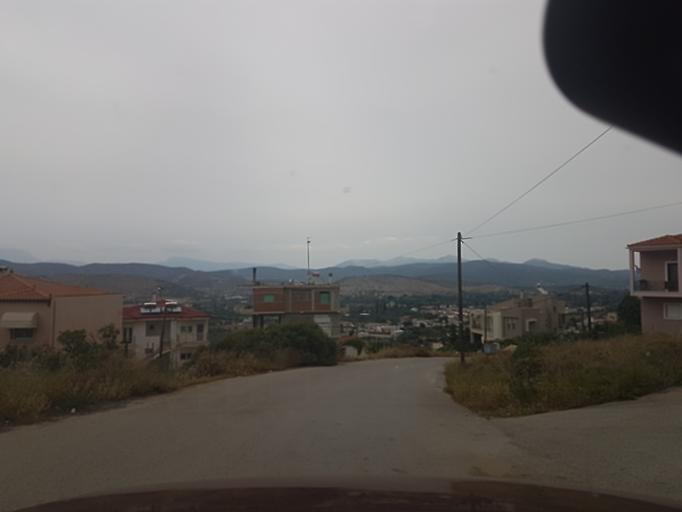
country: GR
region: Central Greece
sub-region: Nomos Evvoias
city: Chalkida
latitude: 38.4625
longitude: 23.6264
